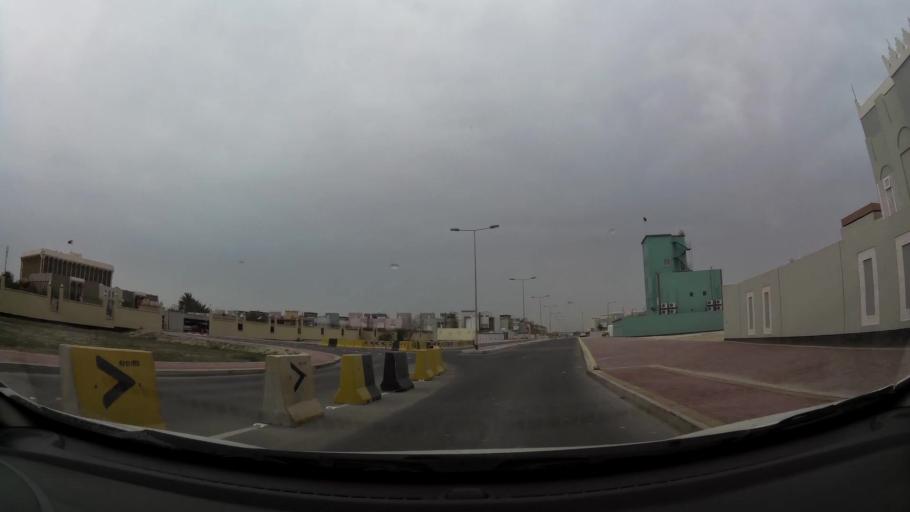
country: BH
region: Northern
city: Madinat `Isa
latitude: 26.1684
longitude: 50.5391
